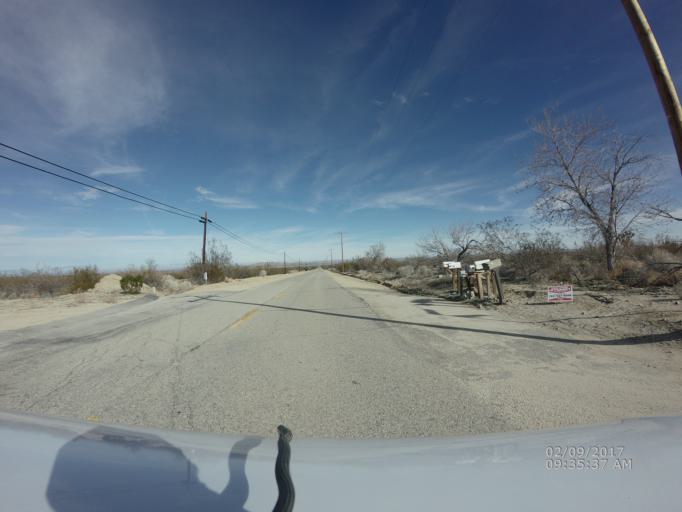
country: US
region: California
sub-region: Los Angeles County
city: Lake Los Angeles
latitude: 34.4952
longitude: -117.8353
